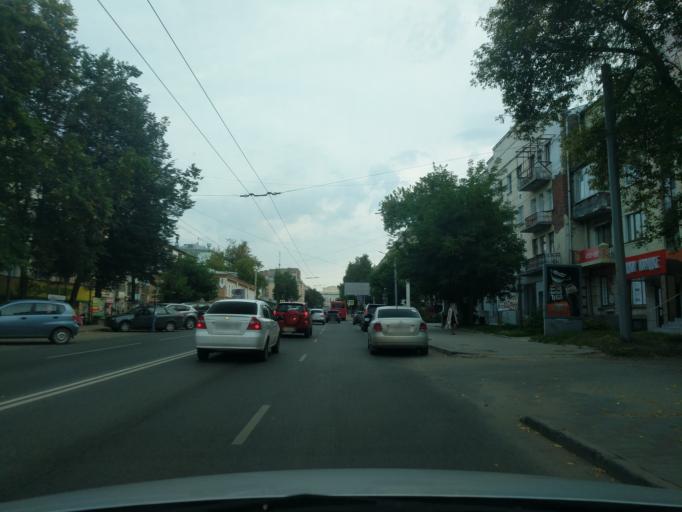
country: RU
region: Kirov
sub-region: Kirovo-Chepetskiy Rayon
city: Kirov
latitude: 58.6112
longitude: 49.6673
